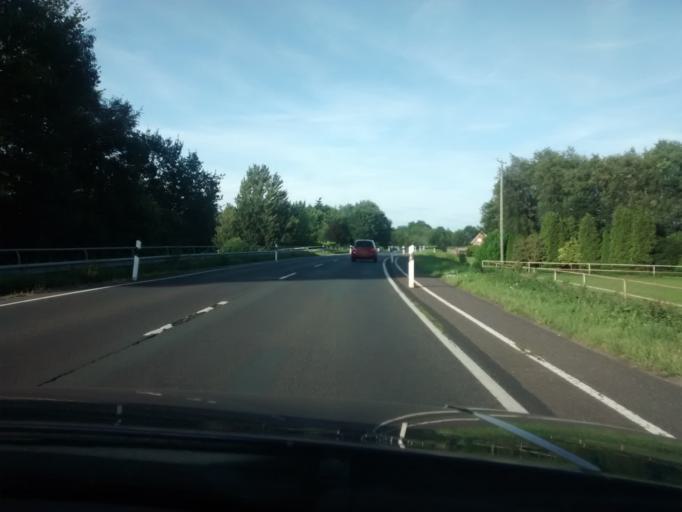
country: DE
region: Lower Saxony
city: Twist
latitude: 52.6509
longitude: 7.1319
